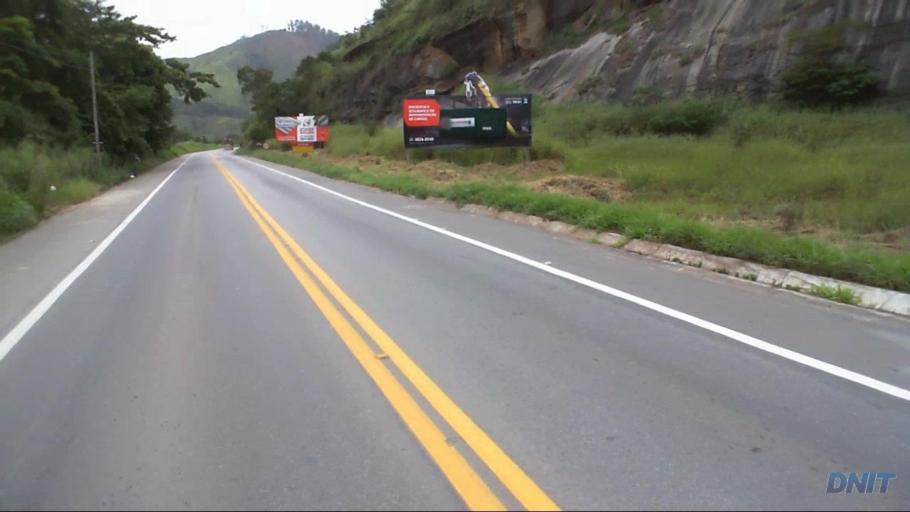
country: BR
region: Minas Gerais
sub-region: Timoteo
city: Timoteo
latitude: -19.5455
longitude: -42.6917
